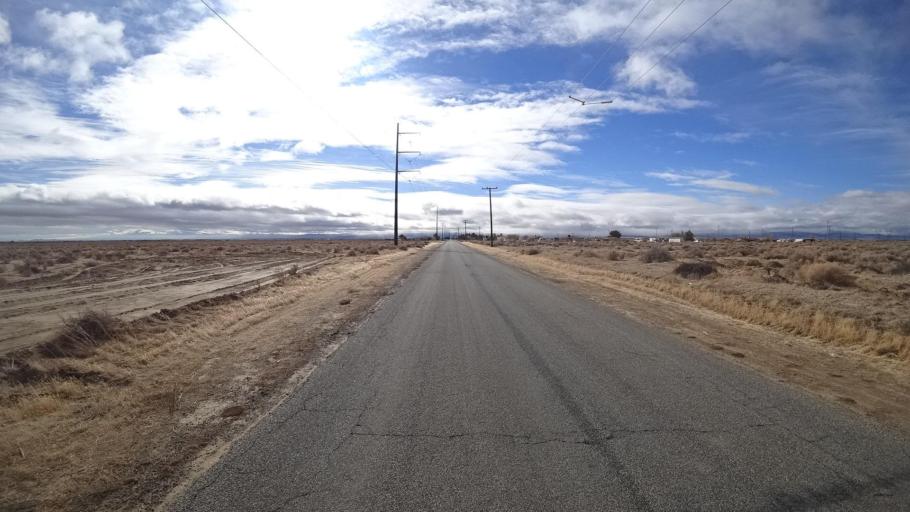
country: US
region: California
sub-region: Kern County
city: Rosamond
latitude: 34.8598
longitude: -118.3089
